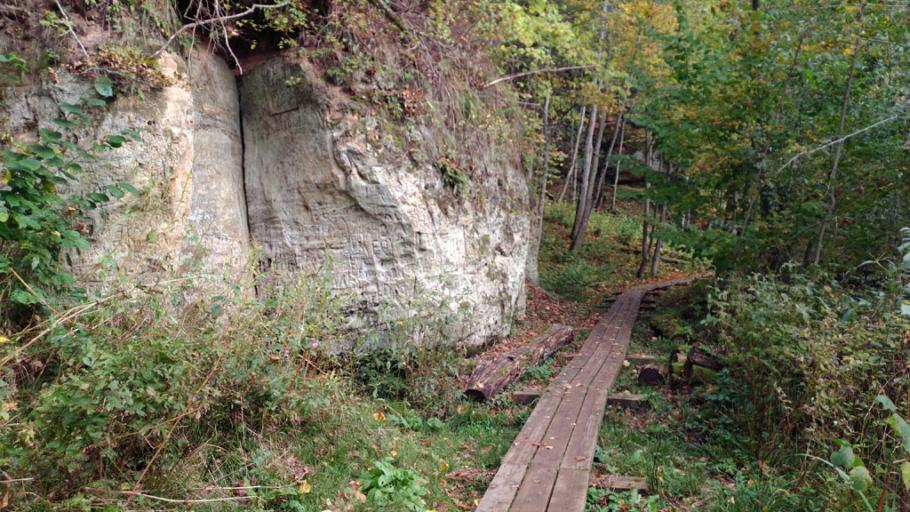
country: LV
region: Sigulda
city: Sigulda
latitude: 57.1504
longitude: 24.8160
